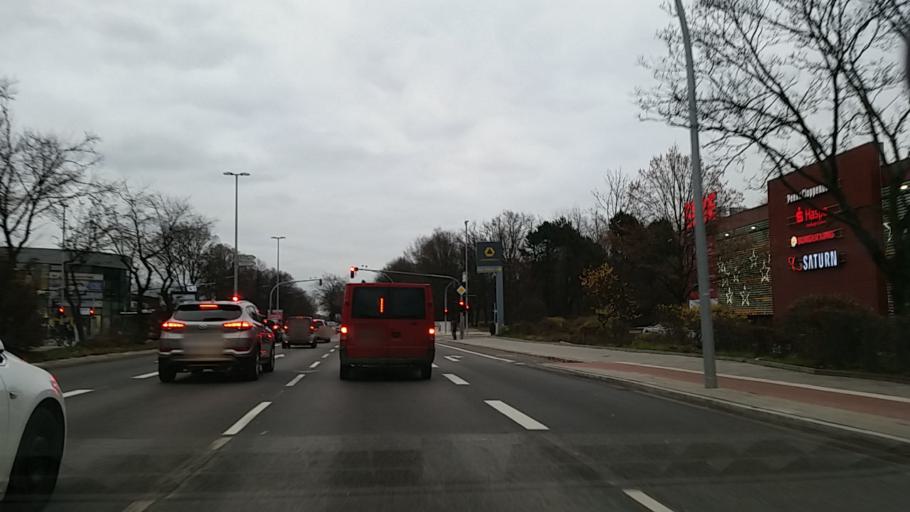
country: DE
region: Hamburg
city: Eidelstedt
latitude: 53.5716
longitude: 9.8641
